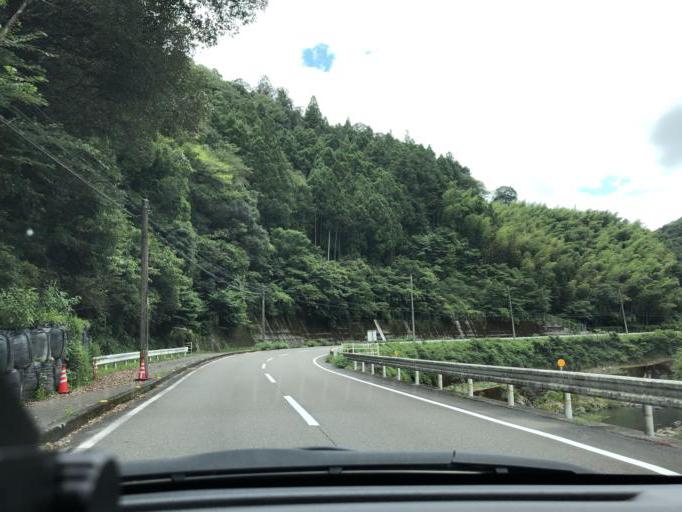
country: JP
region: Kochi
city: Kochi-shi
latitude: 33.6356
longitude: 133.5215
